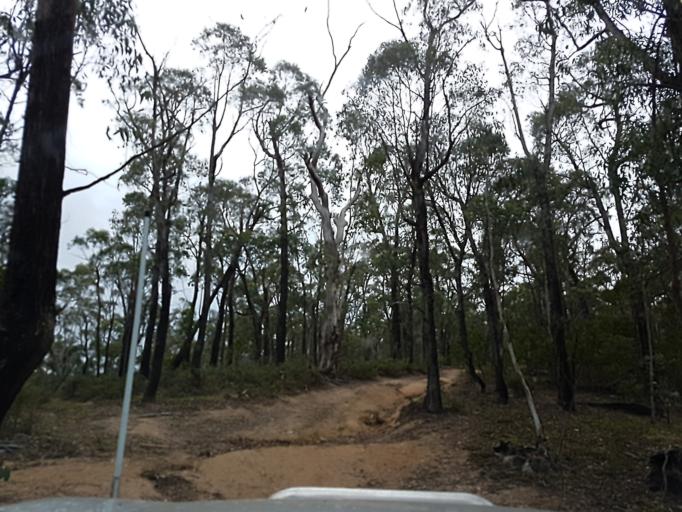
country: AU
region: New South Wales
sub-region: Snowy River
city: Jindabyne
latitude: -36.8616
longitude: 148.3268
